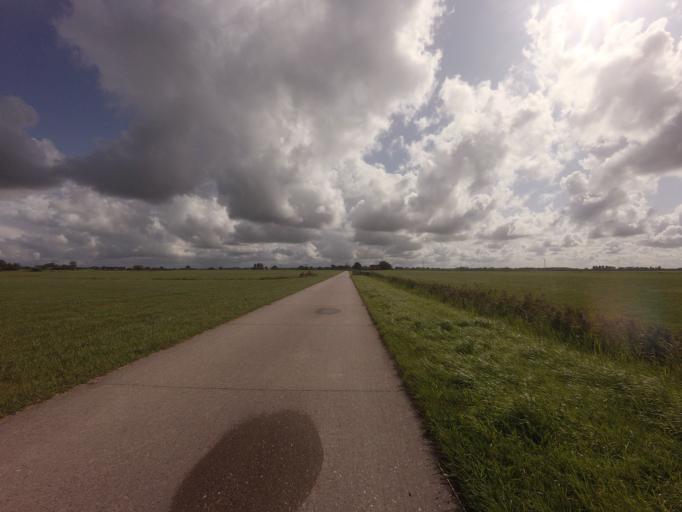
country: NL
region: Friesland
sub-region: Sudwest Fryslan
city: Scharnegoutum
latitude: 53.0693
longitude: 5.6384
